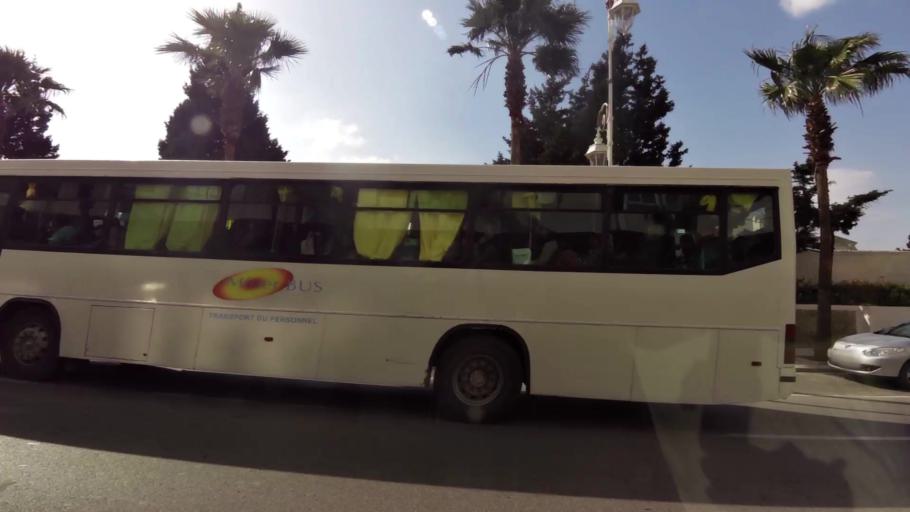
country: MA
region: Tanger-Tetouan
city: Tetouan
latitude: 35.5877
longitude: -5.3465
